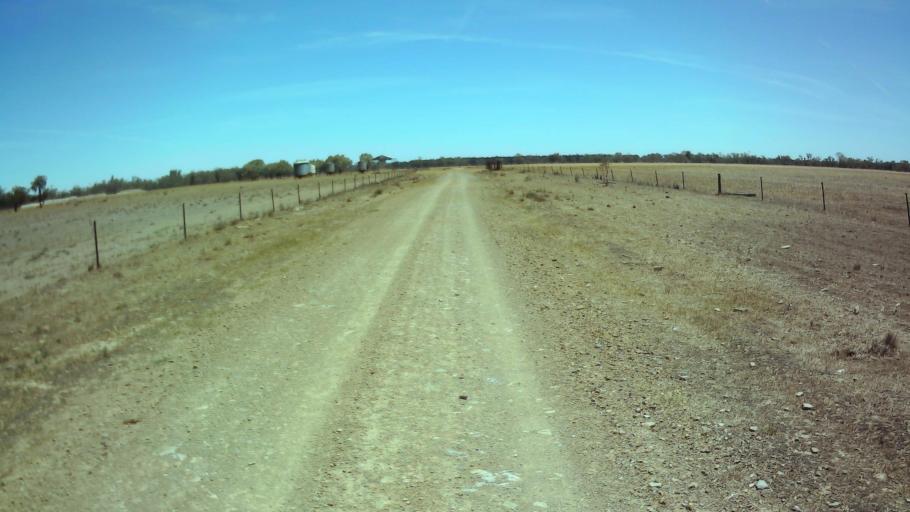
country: AU
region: New South Wales
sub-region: Bland
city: West Wyalong
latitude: -33.8262
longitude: 147.6398
